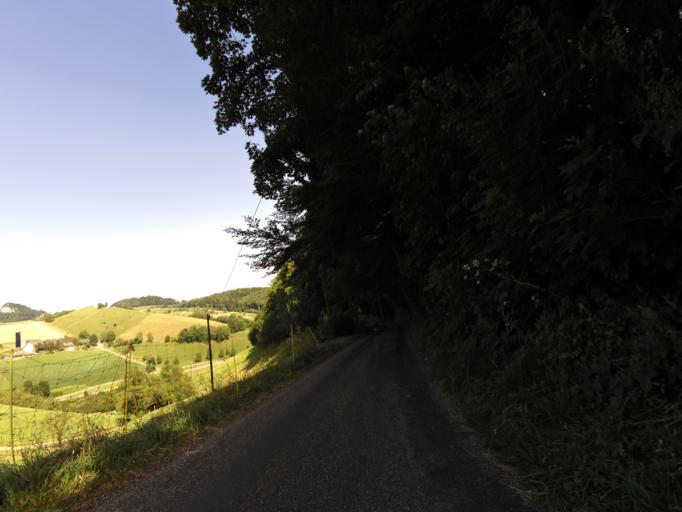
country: CH
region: Basel-Landschaft
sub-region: Bezirk Sissach
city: Laufelfingen
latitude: 47.3828
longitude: 7.8628
